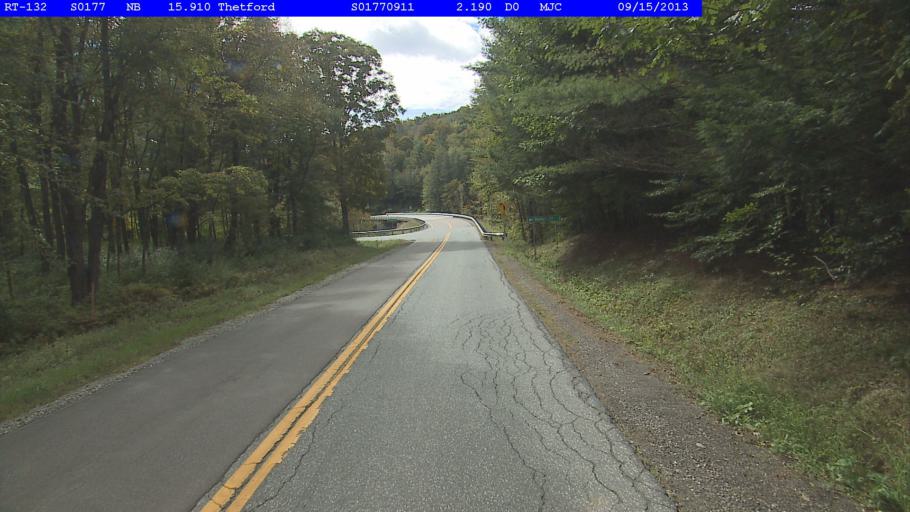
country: US
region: New Hampshire
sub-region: Grafton County
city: Hanover
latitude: 43.8237
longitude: -72.2853
